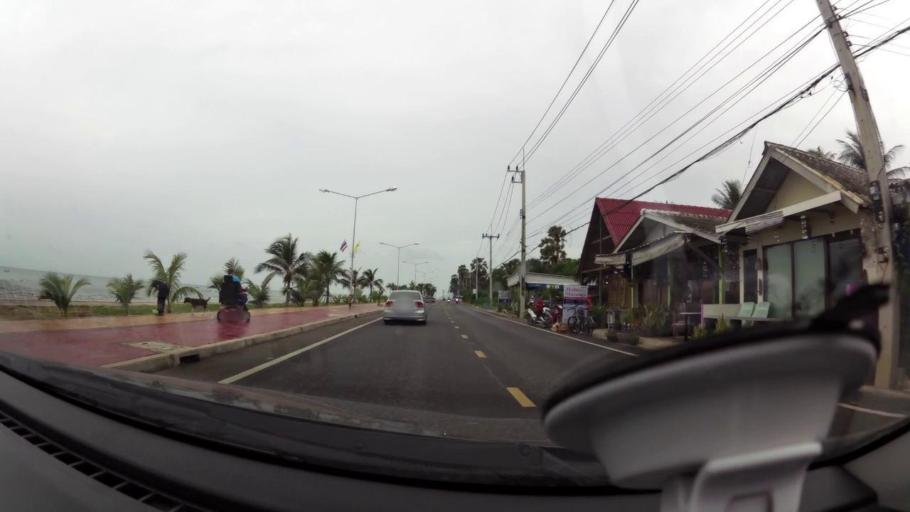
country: TH
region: Prachuap Khiri Khan
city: Pran Buri
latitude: 12.3806
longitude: 99.9999
